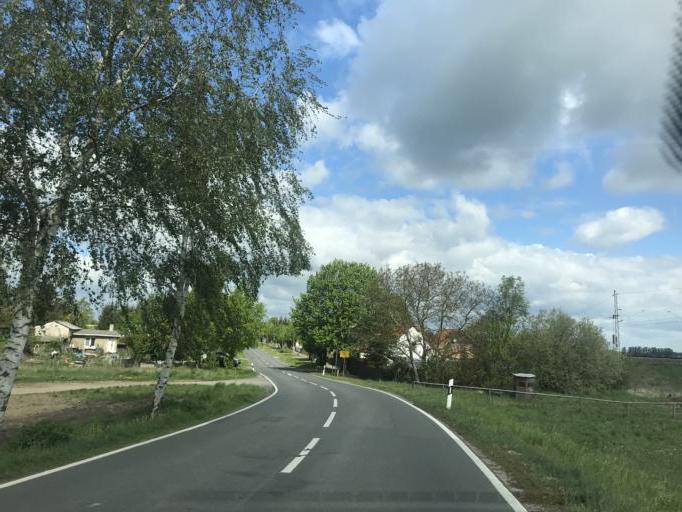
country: DE
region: Brandenburg
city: Gransee
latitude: 52.9329
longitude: 13.1784
